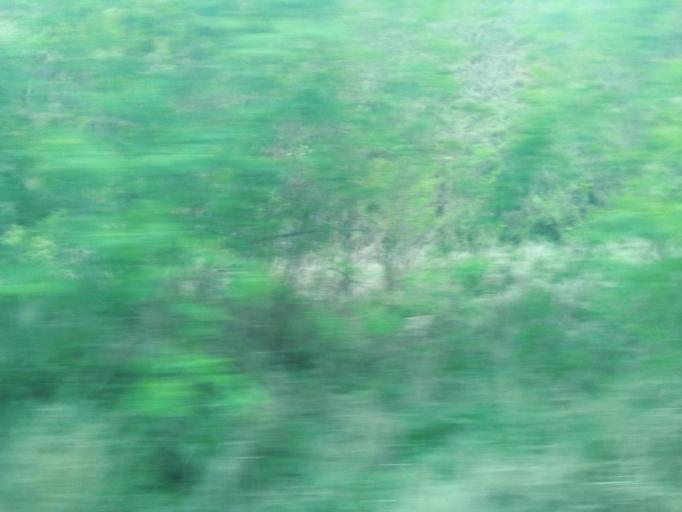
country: BR
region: Minas Gerais
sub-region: Ipaba
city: Ipaba
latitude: -19.4626
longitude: -42.4593
